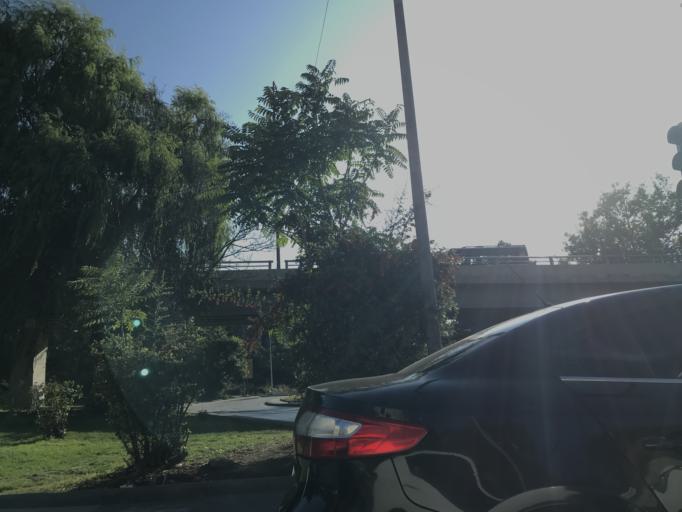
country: TR
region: Ankara
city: Ankara
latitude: 39.9503
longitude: 32.8597
